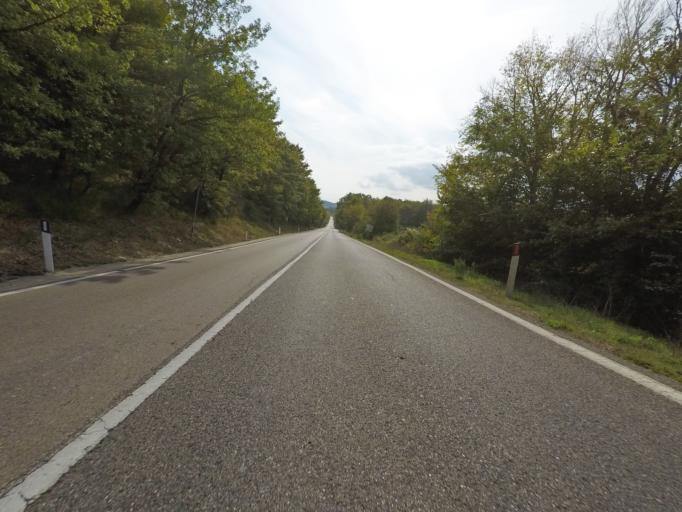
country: IT
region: Tuscany
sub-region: Provincia di Siena
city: Rosia
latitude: 43.1792
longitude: 11.2772
